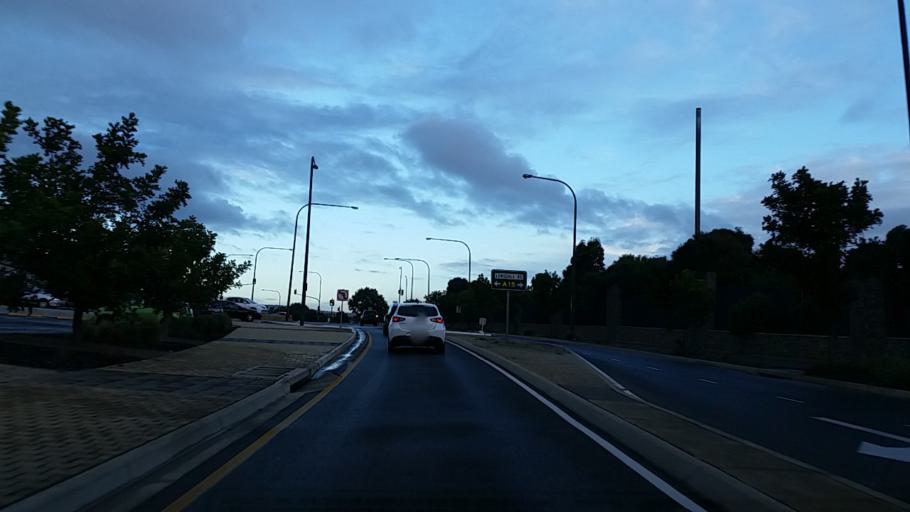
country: AU
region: South Australia
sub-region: Marion
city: Happy Valley
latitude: -35.0784
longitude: 138.5152
